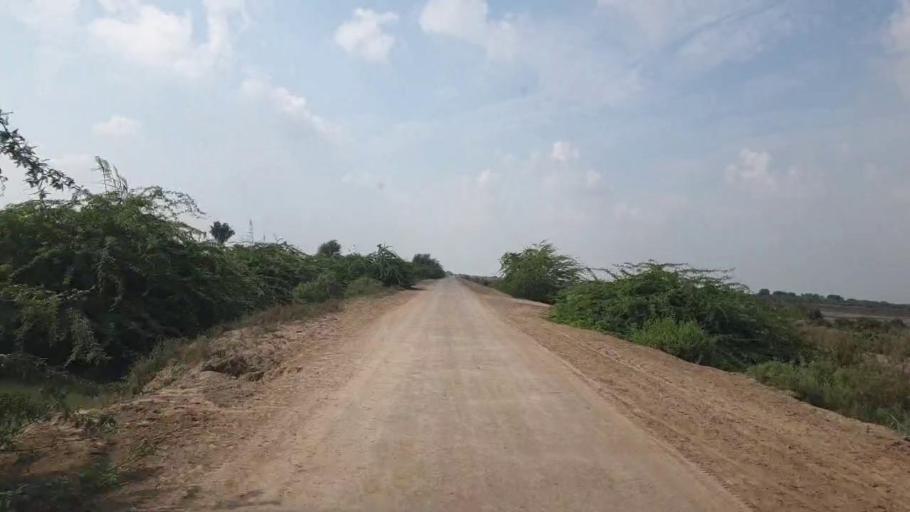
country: PK
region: Sindh
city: Badin
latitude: 24.5065
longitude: 68.6373
